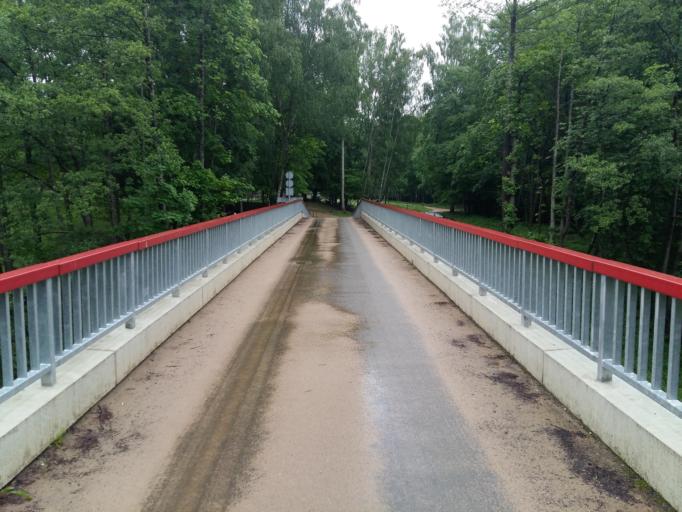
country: LT
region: Alytaus apskritis
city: Druskininkai
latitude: 53.9550
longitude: 23.8343
